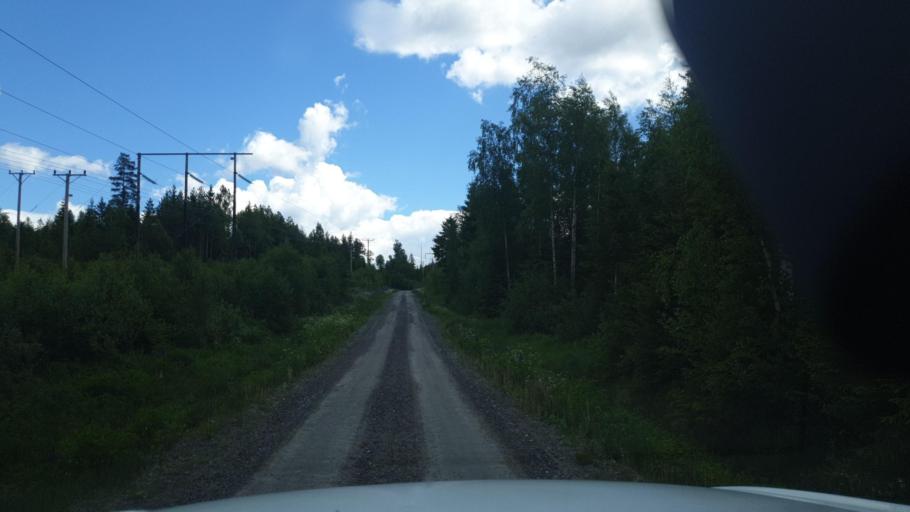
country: SE
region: Vaermland
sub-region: Arvika Kommun
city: Arvika
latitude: 59.5376
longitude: 12.4135
